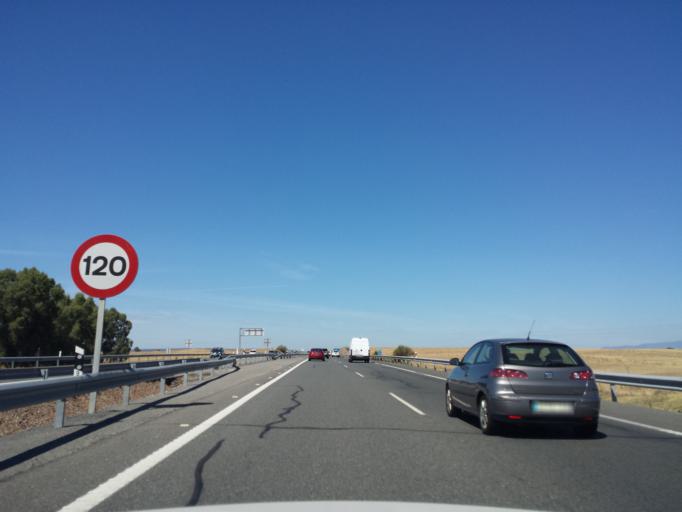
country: ES
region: Extremadura
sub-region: Provincia de Caceres
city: Berrocalejo
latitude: 39.8949
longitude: -5.3538
